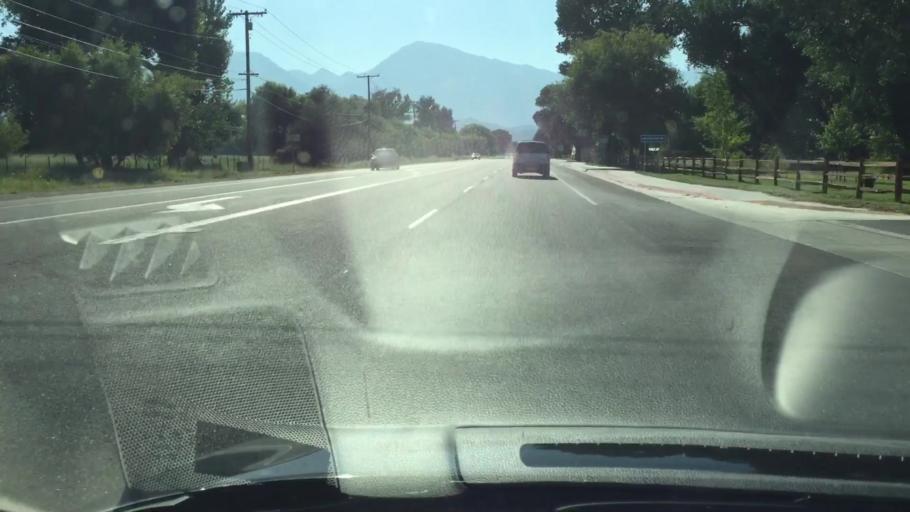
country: US
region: California
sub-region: Inyo County
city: Bishop
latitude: 37.3618
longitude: -118.4151
